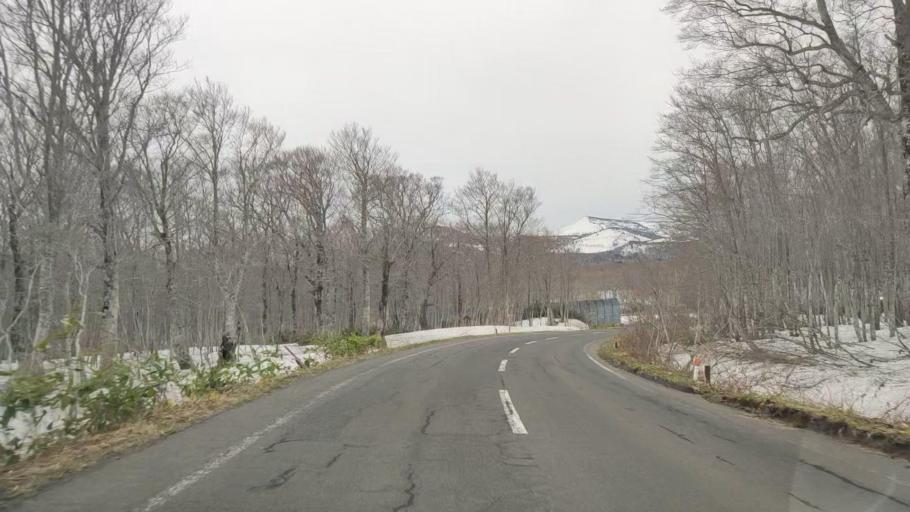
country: JP
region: Aomori
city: Aomori Shi
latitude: 40.6345
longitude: 140.9294
